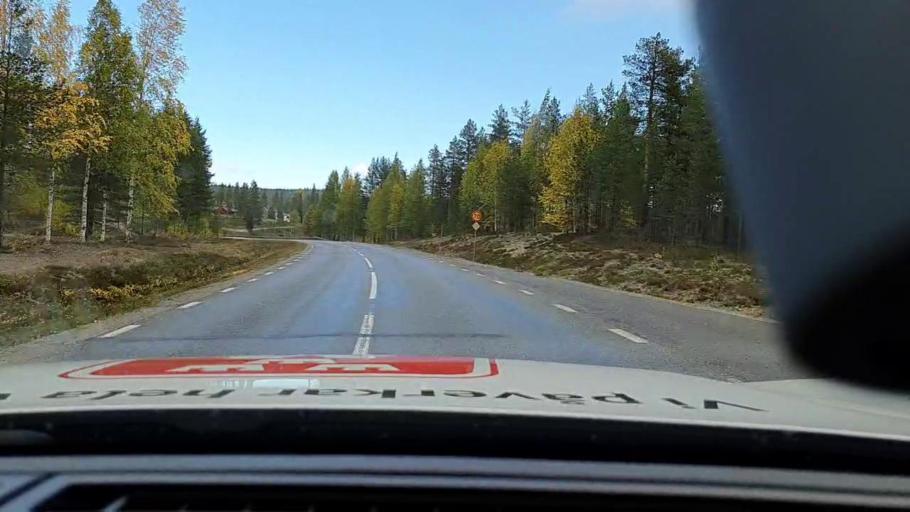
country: SE
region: Vaesterbotten
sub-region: Norsjo Kommun
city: Norsjoe
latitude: 64.9683
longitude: 19.7144
